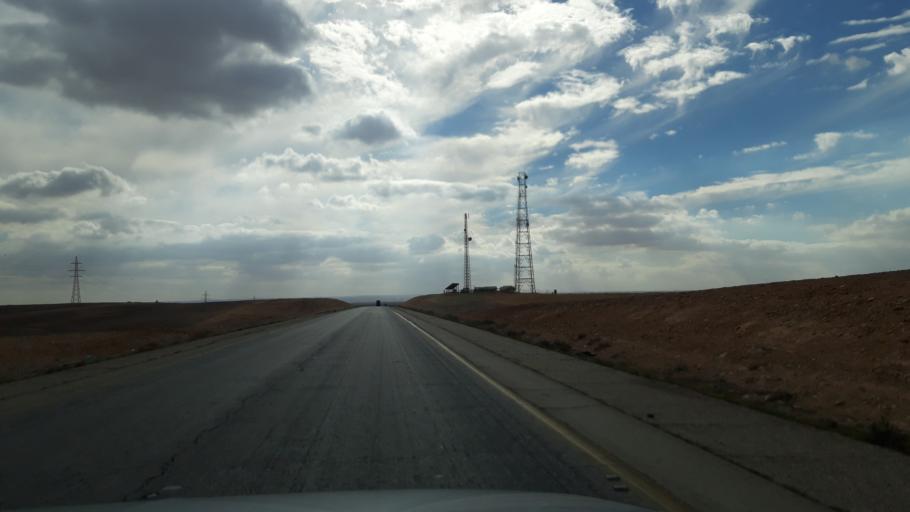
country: JO
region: Amman
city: Al Azraq ash Shamali
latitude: 31.7380
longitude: 36.5228
